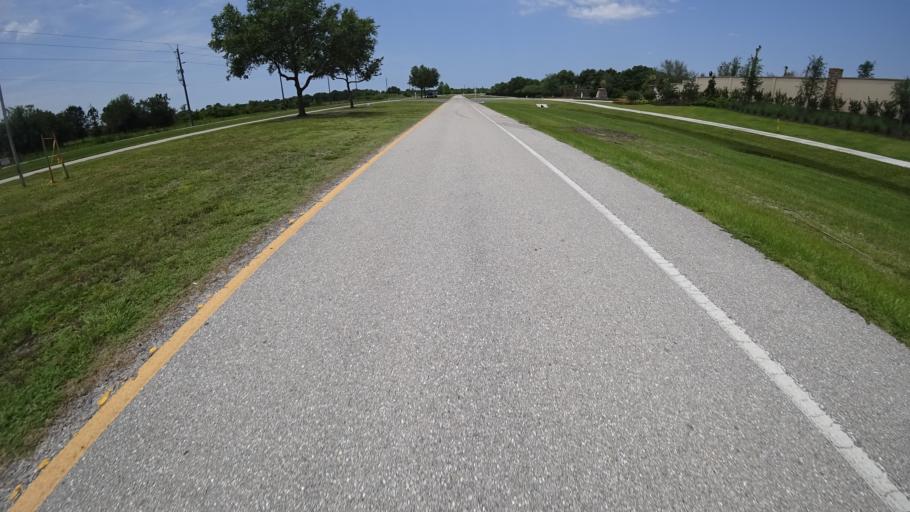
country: US
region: Florida
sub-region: Sarasota County
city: The Meadows
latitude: 27.3862
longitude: -82.3671
